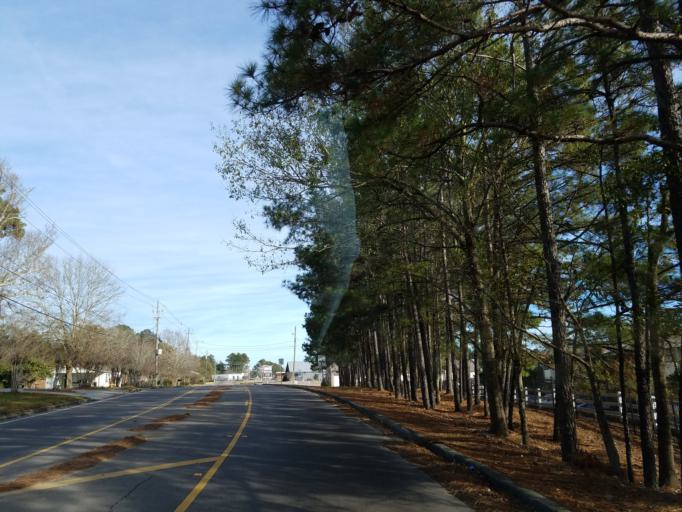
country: US
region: Mississippi
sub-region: Lamar County
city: Arnold Line
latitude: 31.3359
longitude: -89.3502
